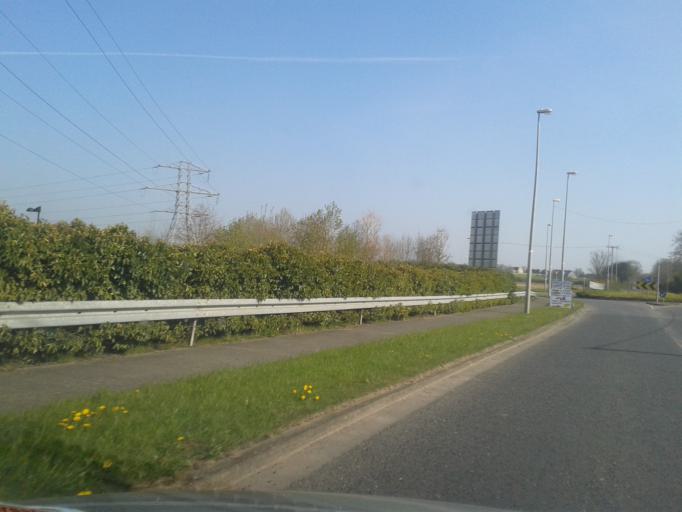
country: IE
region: Leinster
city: Balrothery
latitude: 53.5719
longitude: -6.2082
